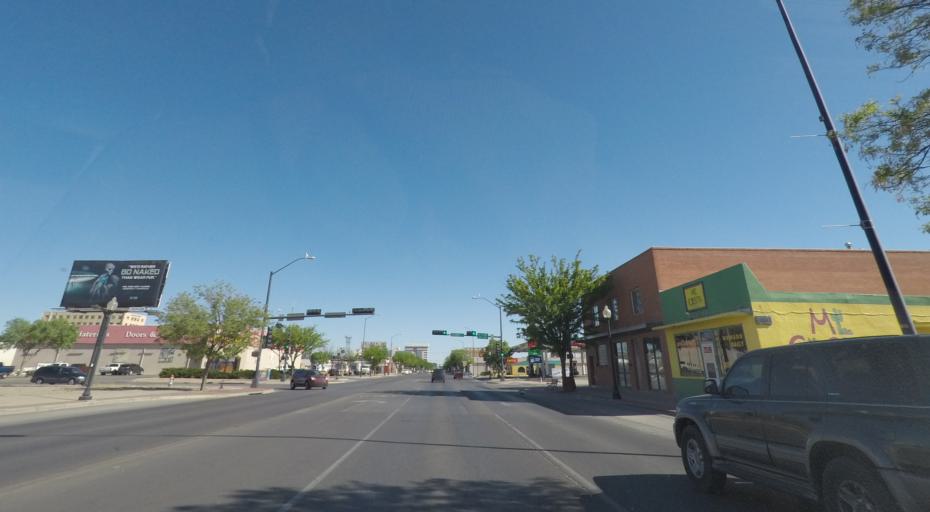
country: US
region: New Mexico
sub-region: Chaves County
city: Roswell
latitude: 33.3904
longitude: -104.5227
